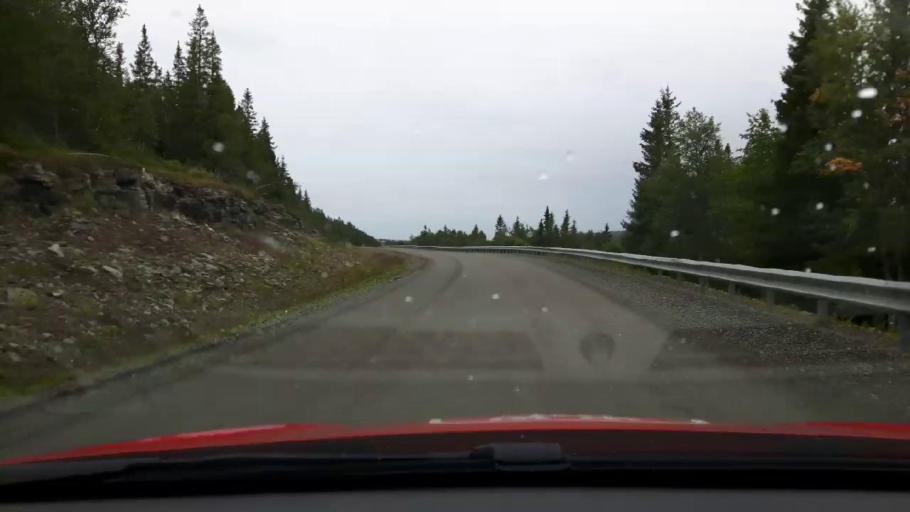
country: NO
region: Nord-Trondelag
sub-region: Meraker
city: Meraker
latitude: 63.5352
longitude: 12.3853
